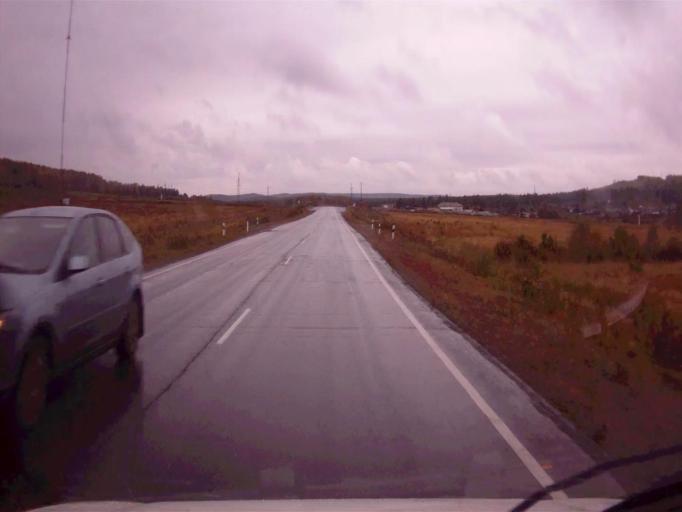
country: RU
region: Chelyabinsk
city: Verkhniy Ufaley
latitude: 56.0004
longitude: 60.3301
